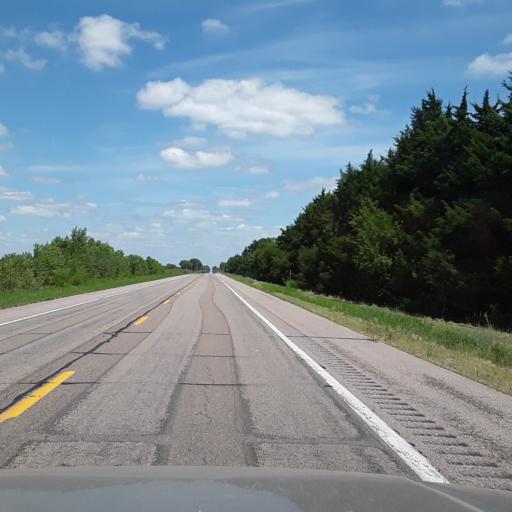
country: US
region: Nebraska
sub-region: Polk County
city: Osceola
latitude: 41.3624
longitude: -97.5540
